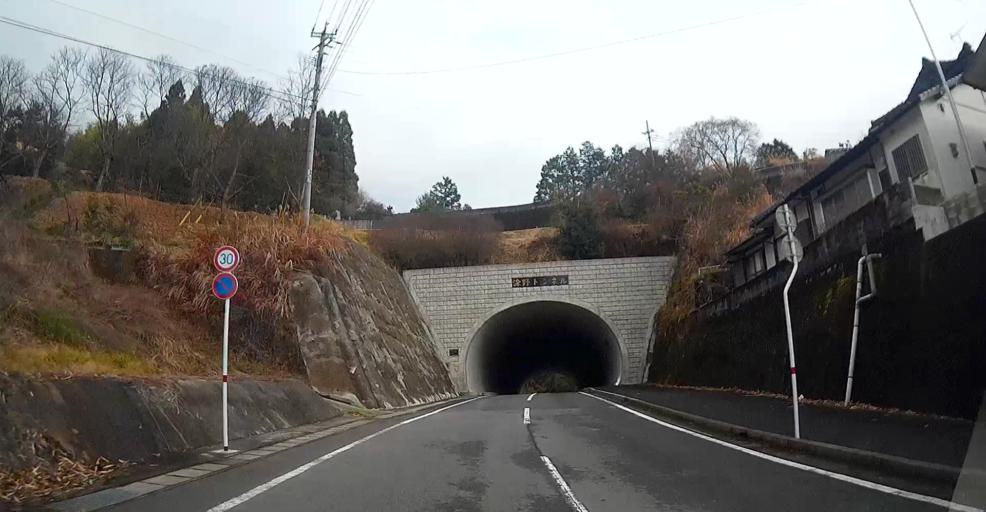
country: JP
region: Kumamoto
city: Ozu
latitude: 32.6809
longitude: 130.9889
